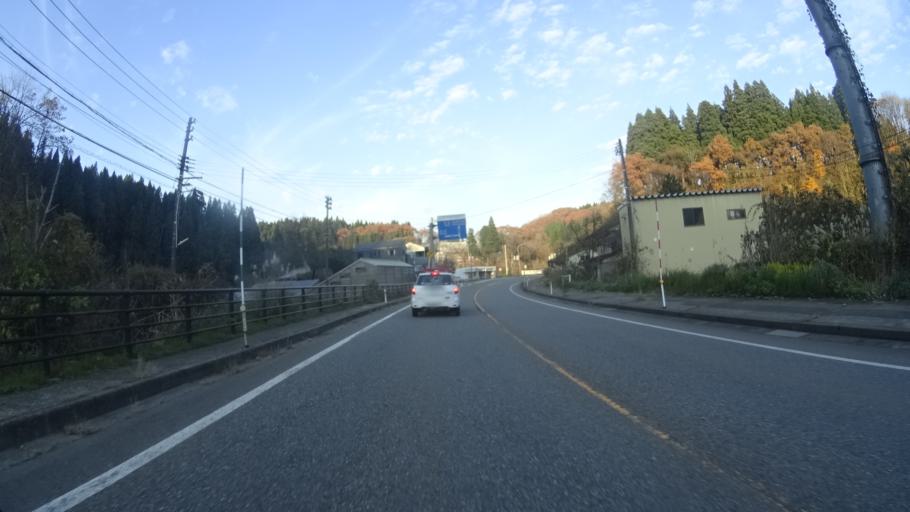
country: JP
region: Niigata
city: Ojiya
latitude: 37.4124
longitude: 138.7040
